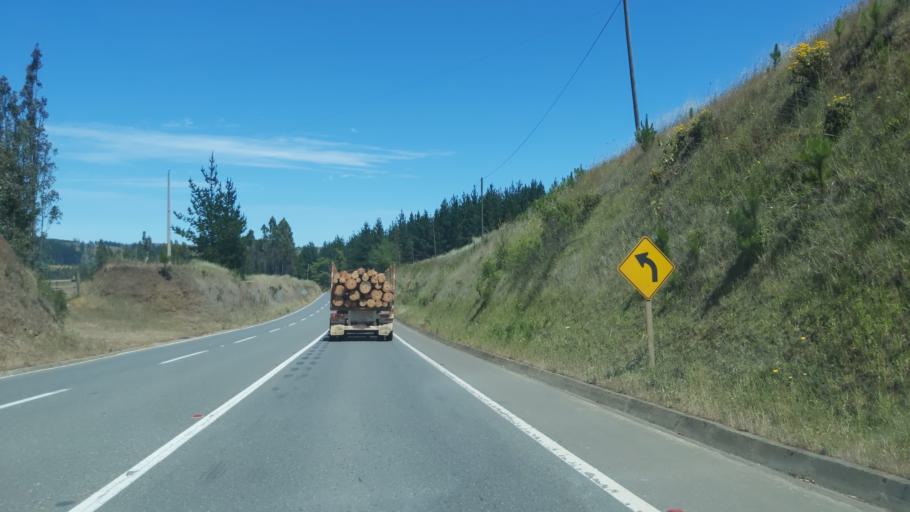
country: CL
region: Maule
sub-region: Provincia de Talca
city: Constitucion
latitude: -35.1507
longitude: -72.2159
